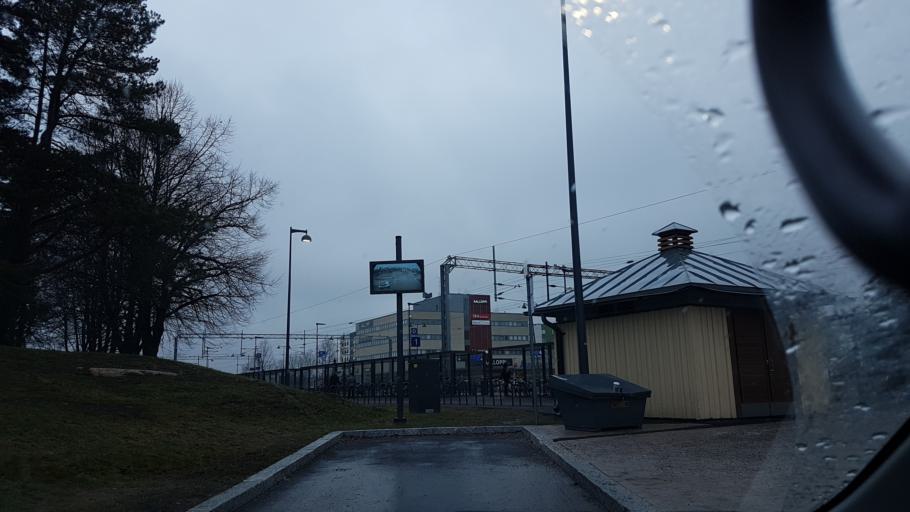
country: FI
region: Uusimaa
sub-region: Helsinki
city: Jaervenpaeae
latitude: 60.4738
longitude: 25.0900
